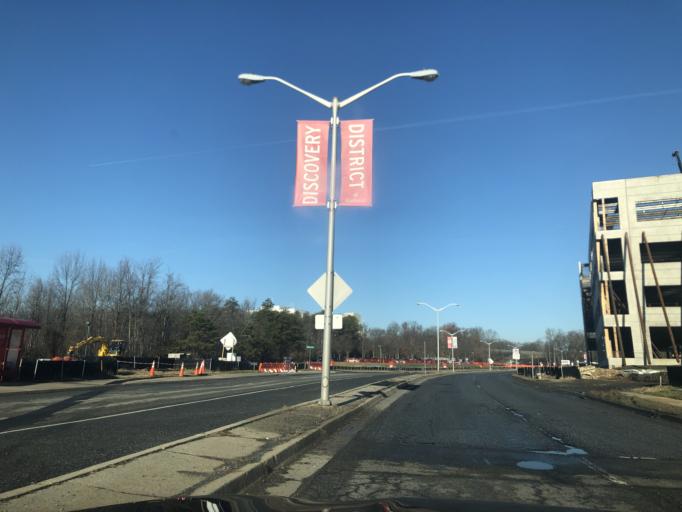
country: US
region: Maryland
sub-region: Prince George's County
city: Riverdale Park
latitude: 38.9700
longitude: -76.9269
